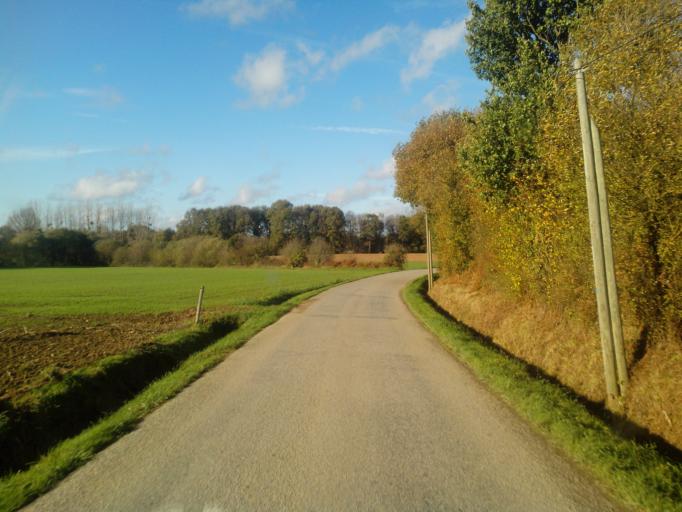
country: FR
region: Brittany
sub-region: Departement du Morbihan
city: Guilliers
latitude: 48.0711
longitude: -2.4100
